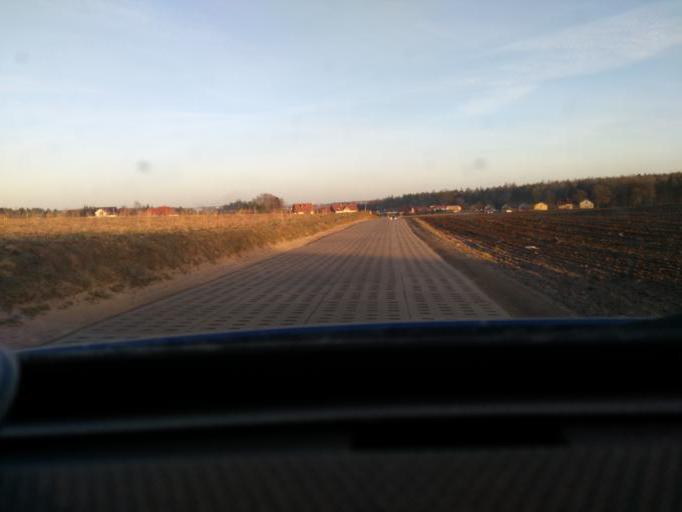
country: PL
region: Pomeranian Voivodeship
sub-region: Powiat kartuski
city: Banino
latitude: 54.3803
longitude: 18.4012
